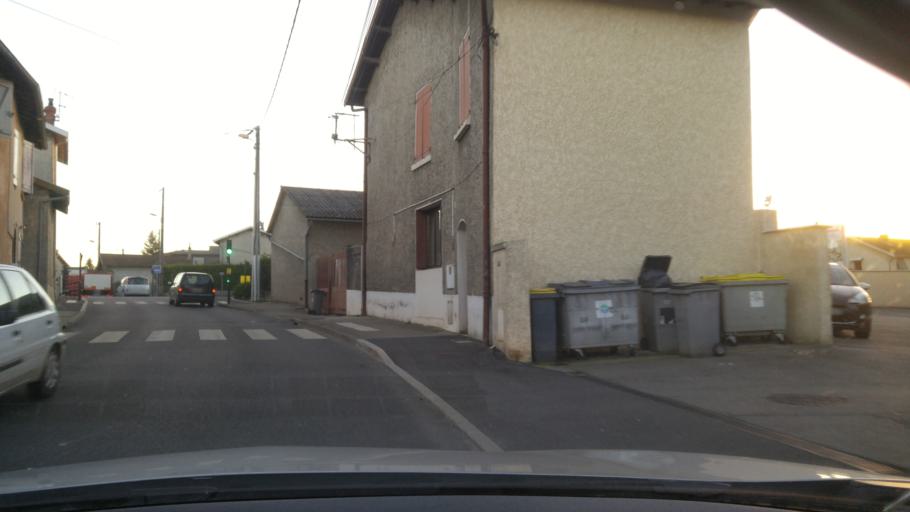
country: FR
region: Rhone-Alpes
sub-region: Departement de l'Isere
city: Tignieu-Jameyzieu
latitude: 45.7361
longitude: 5.1873
